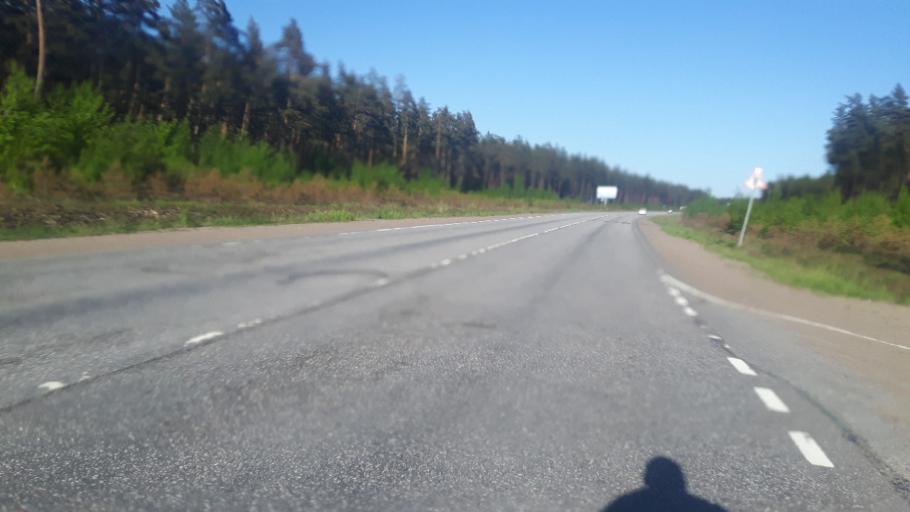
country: RU
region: Leningrad
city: Lebyazh'ye
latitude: 60.1681
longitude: 29.2343
